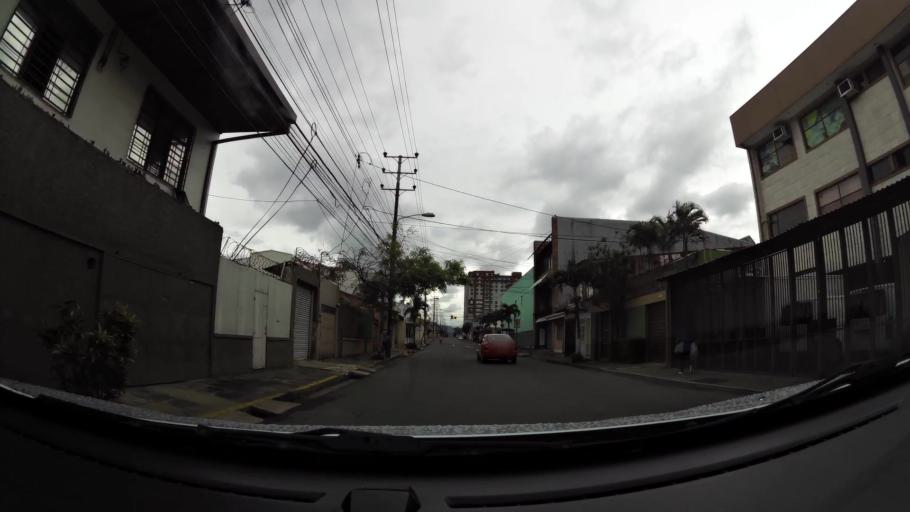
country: CR
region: San Jose
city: San Jose
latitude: 9.9328
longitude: -84.0955
